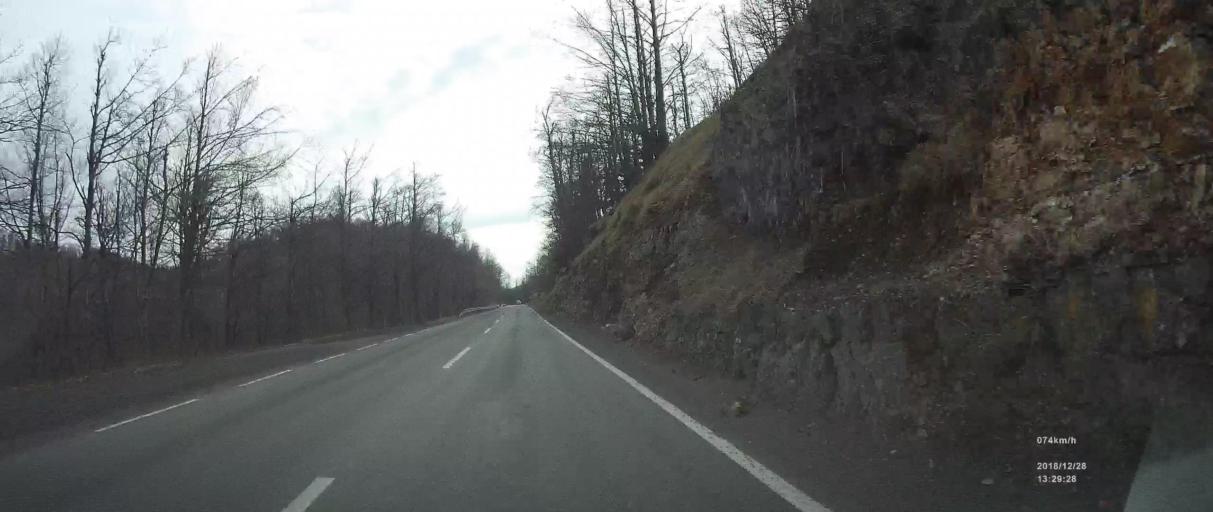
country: HR
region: Primorsko-Goranska
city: Hreljin
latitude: 45.3607
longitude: 14.6288
